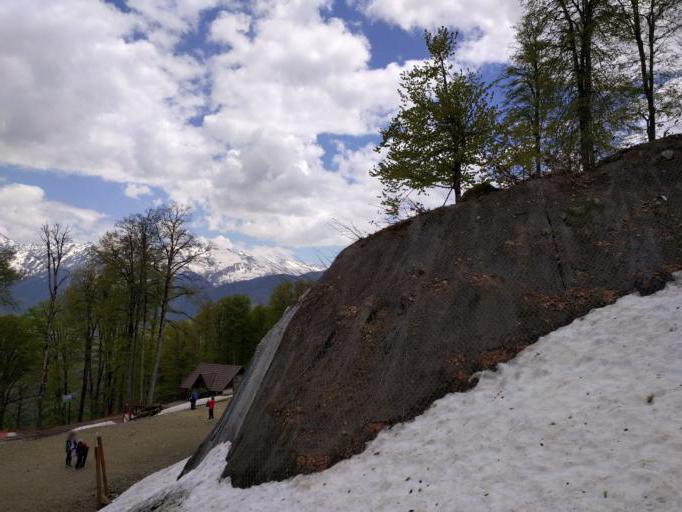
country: RU
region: Krasnodarskiy
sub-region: Sochi City
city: Krasnaya Polyana
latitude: 43.6441
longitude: 40.3150
